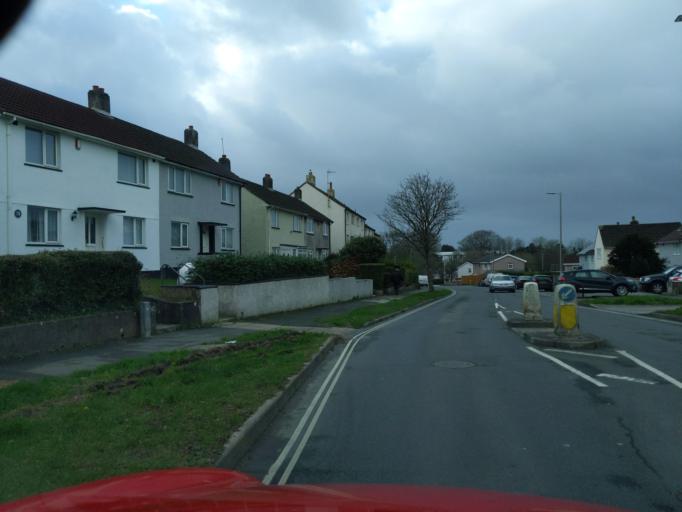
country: GB
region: England
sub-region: Plymouth
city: Plymouth
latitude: 50.3973
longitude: -4.1610
